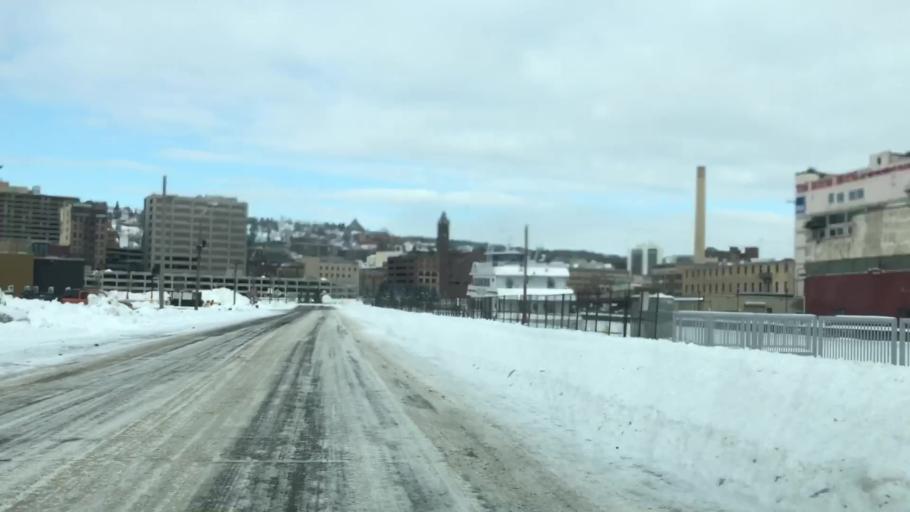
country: US
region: Minnesota
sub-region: Saint Louis County
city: Duluth
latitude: 46.7817
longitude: -92.0968
